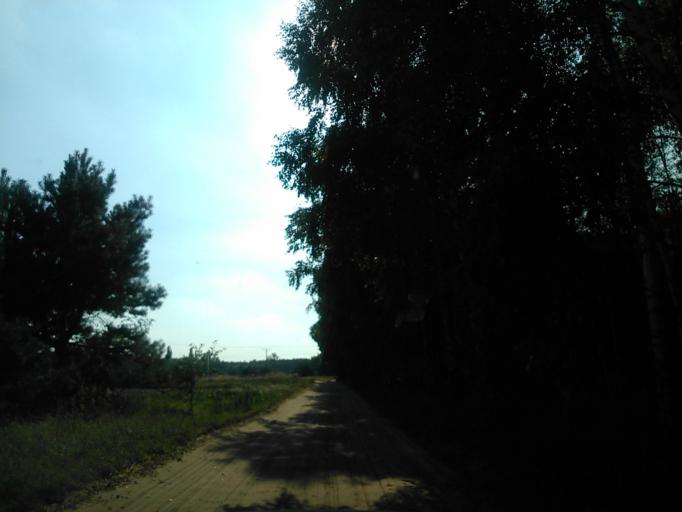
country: PL
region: Kujawsko-Pomorskie
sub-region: Powiat golubsko-dobrzynski
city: Golub-Dobrzyn
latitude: 53.1146
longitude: 19.0775
